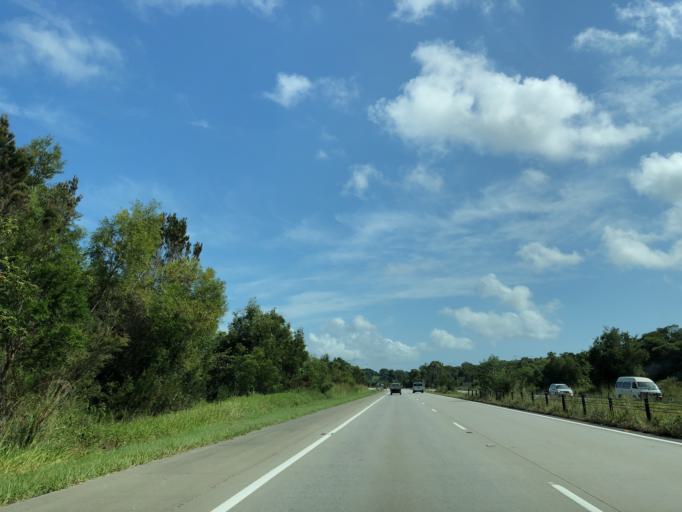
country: AU
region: New South Wales
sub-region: Byron Shire
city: Brunswick Heads
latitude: -28.5844
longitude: 153.5445
